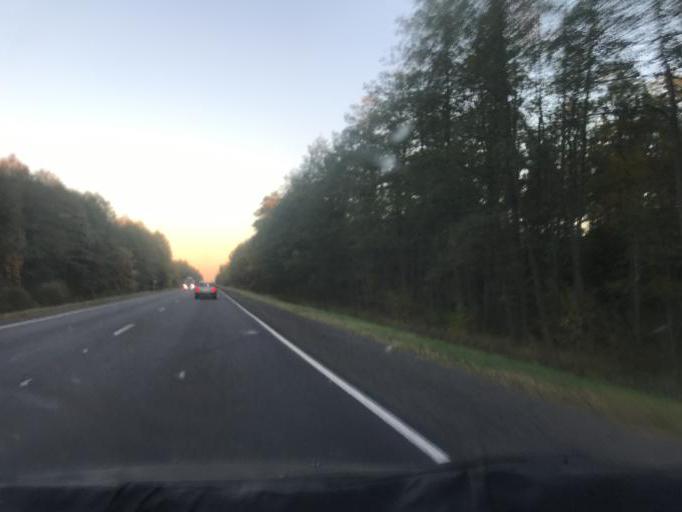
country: BY
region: Gomel
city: Mazyr
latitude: 52.1739
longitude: 29.1921
